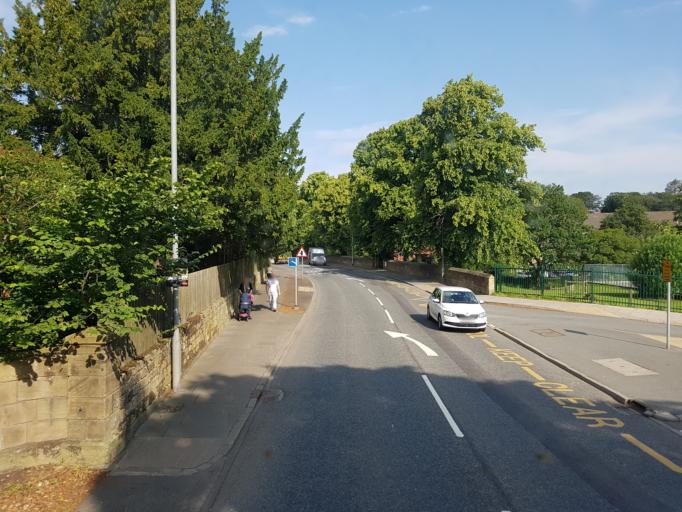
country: GB
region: England
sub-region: Northumberland
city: Alnwick
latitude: 55.4093
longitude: -1.6958
